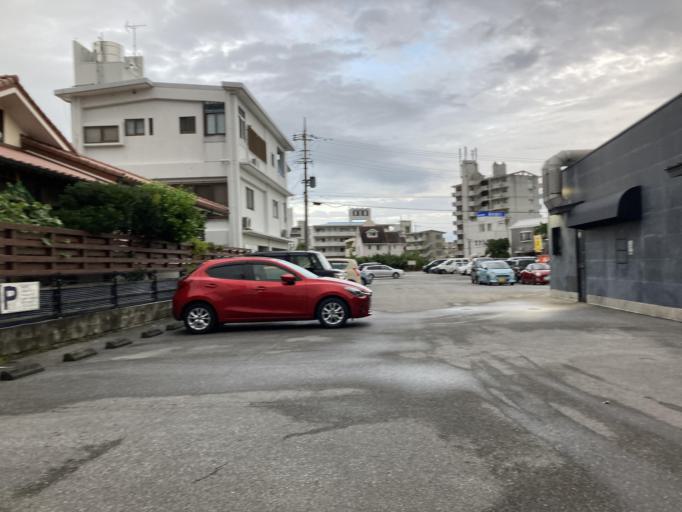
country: JP
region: Okinawa
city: Okinawa
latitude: 26.3187
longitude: 127.8256
